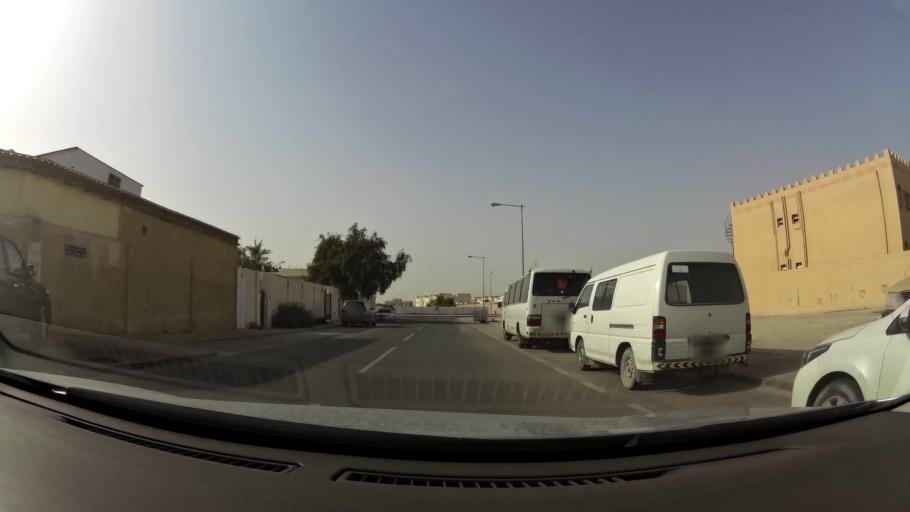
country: QA
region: Baladiyat ar Rayyan
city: Ar Rayyan
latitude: 25.2387
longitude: 51.4402
